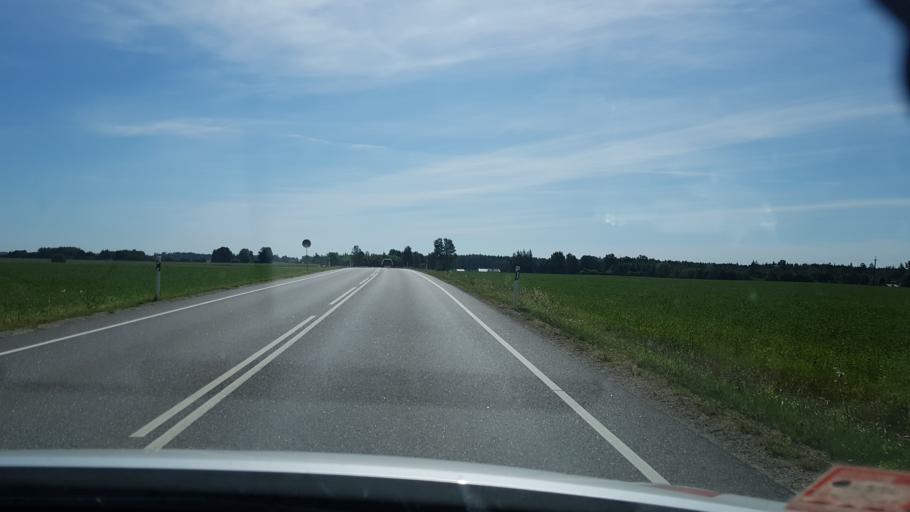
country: EE
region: Tartu
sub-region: Tartu linn
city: Tartu
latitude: 58.4291
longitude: 26.8480
